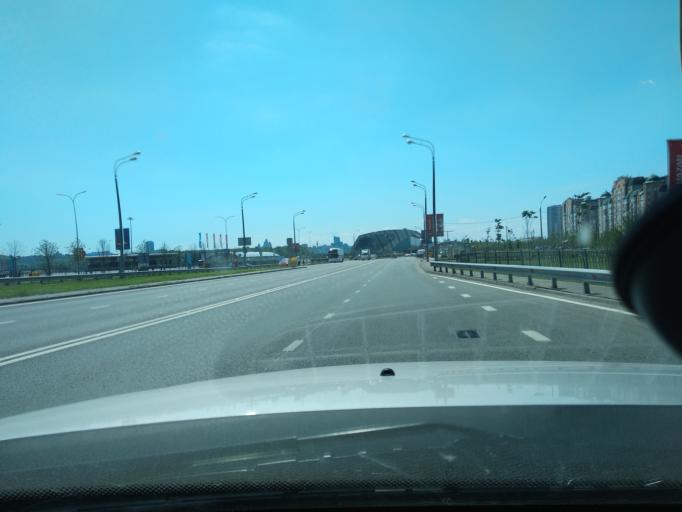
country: RU
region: Tatarstan
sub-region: Gorod Kazan'
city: Kazan
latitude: 55.8223
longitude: 49.1561
